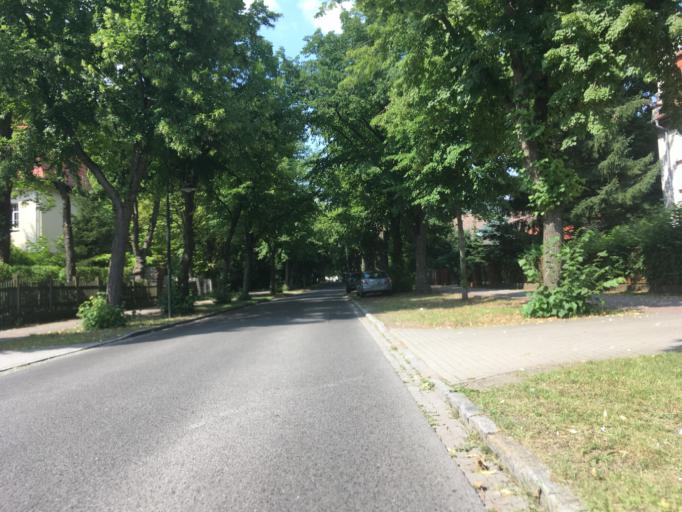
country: DE
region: Brandenburg
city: Zeuthen
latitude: 52.3620
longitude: 13.6253
